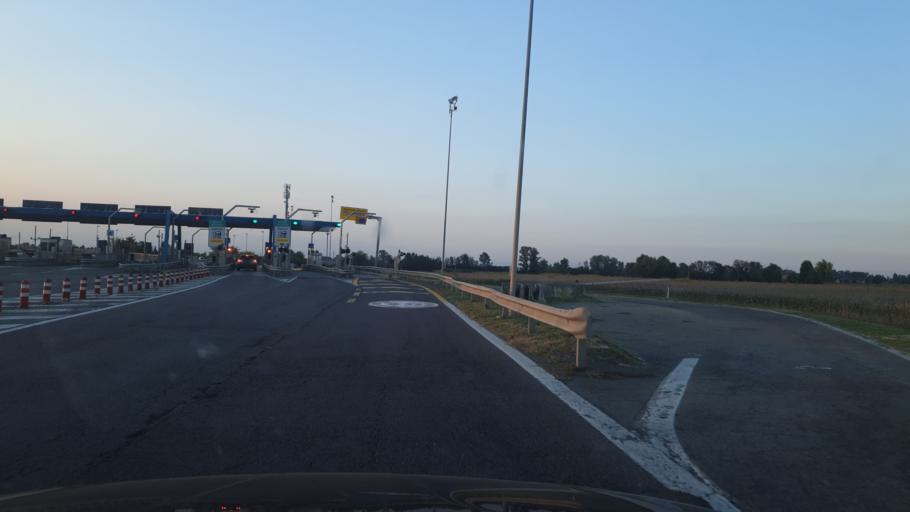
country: IT
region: Emilia-Romagna
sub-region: Provincia di Bologna
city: Progresso
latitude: 44.5877
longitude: 11.4024
